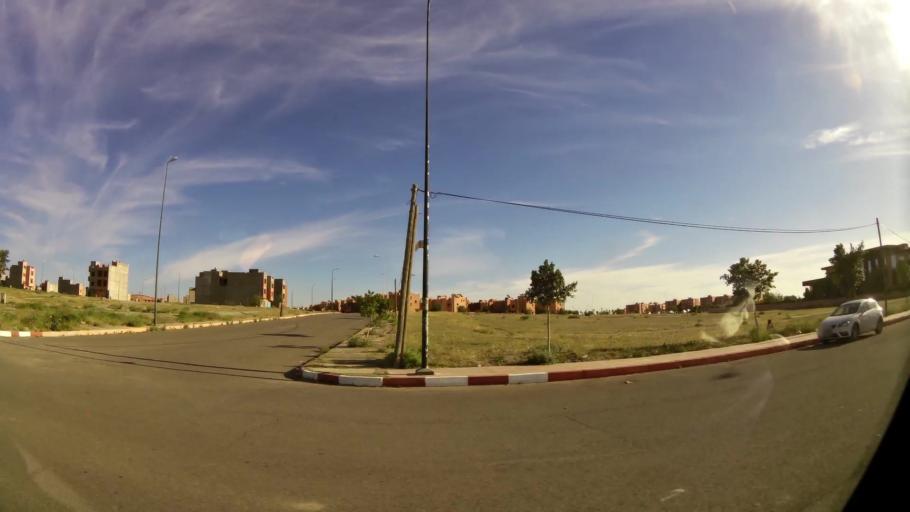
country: MA
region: Marrakech-Tensift-Al Haouz
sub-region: Marrakech
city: Marrakesh
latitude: 31.7541
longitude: -8.1081
